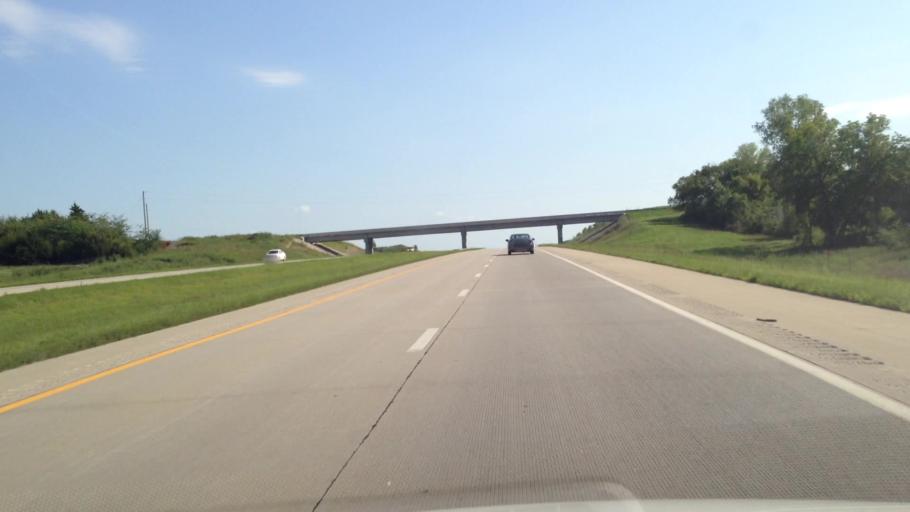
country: US
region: Kansas
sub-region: Linn County
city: Pleasanton
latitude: 38.1124
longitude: -94.7137
